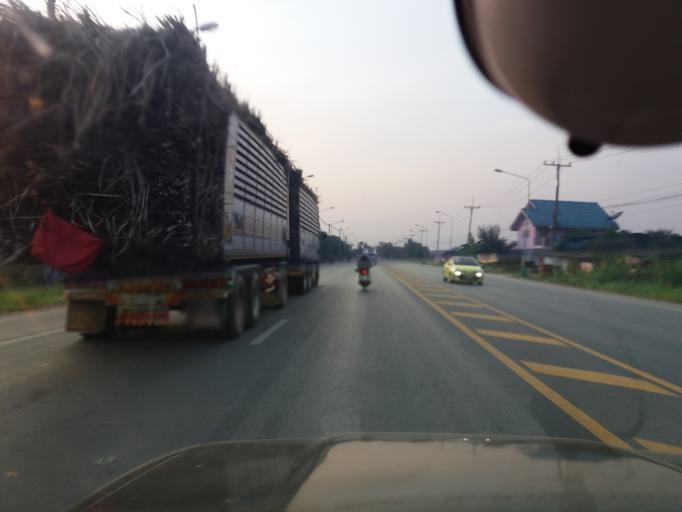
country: TH
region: Sing Buri
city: Sing Buri
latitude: 14.8854
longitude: 100.3757
